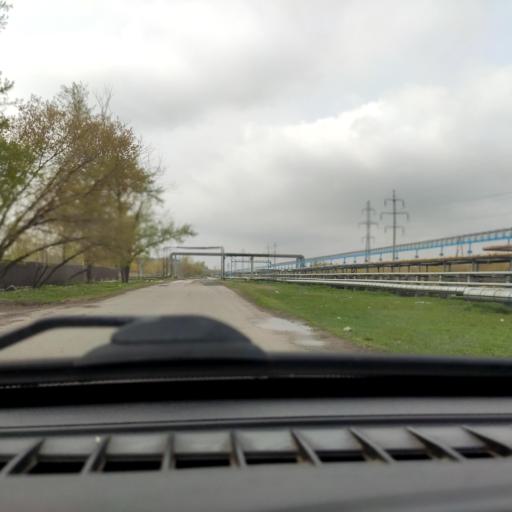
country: RU
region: Samara
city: Tol'yatti
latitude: 53.5384
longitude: 49.4839
